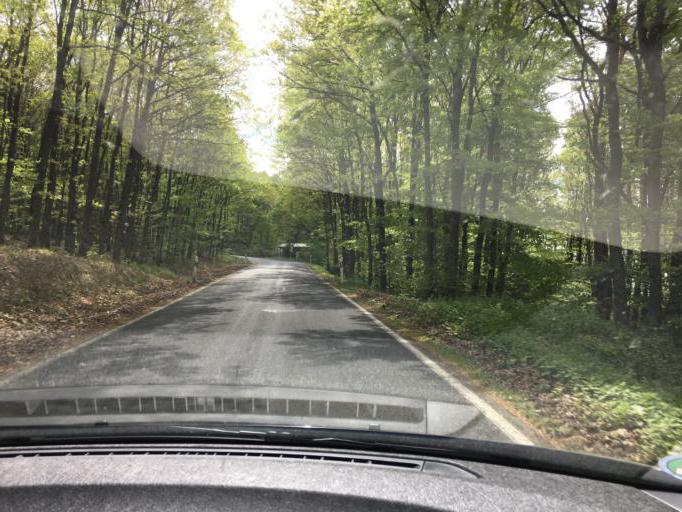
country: DE
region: Rheinland-Pfalz
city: Lind
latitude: 50.4933
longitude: 6.9176
